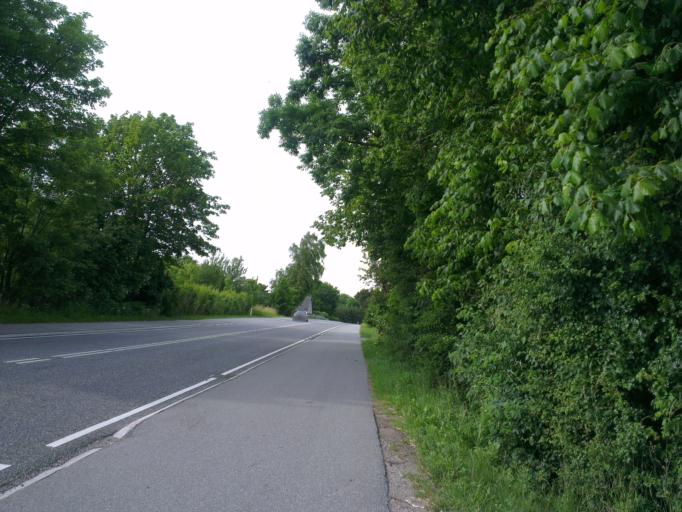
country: DK
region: Capital Region
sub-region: Frederikssund Kommune
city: Skibby
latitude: 55.7730
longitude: 11.9601
